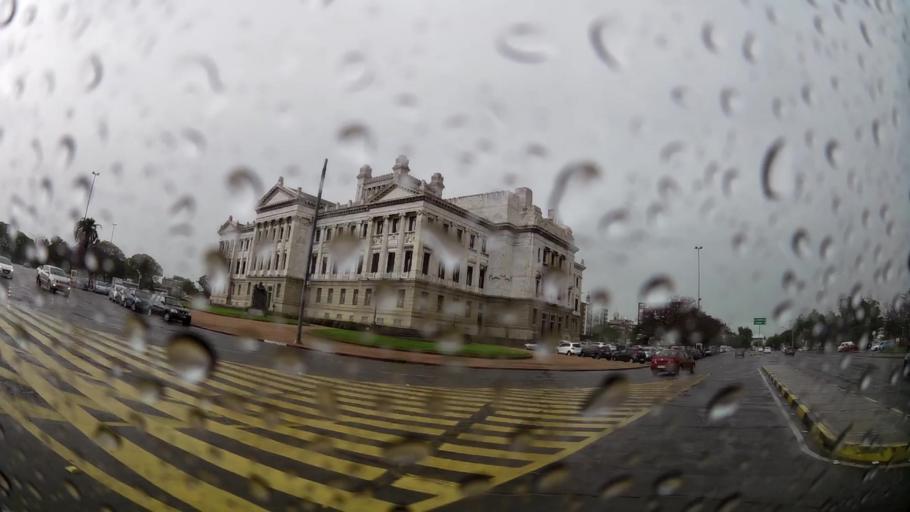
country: UY
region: Montevideo
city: Montevideo
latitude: -34.8902
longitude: -56.1878
